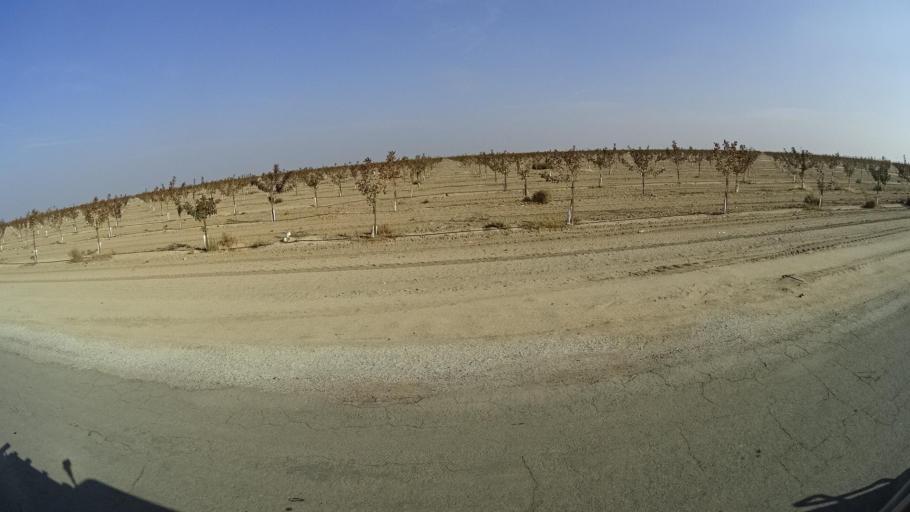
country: US
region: California
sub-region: Tulare County
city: Richgrove
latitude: 35.7842
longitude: -119.1163
